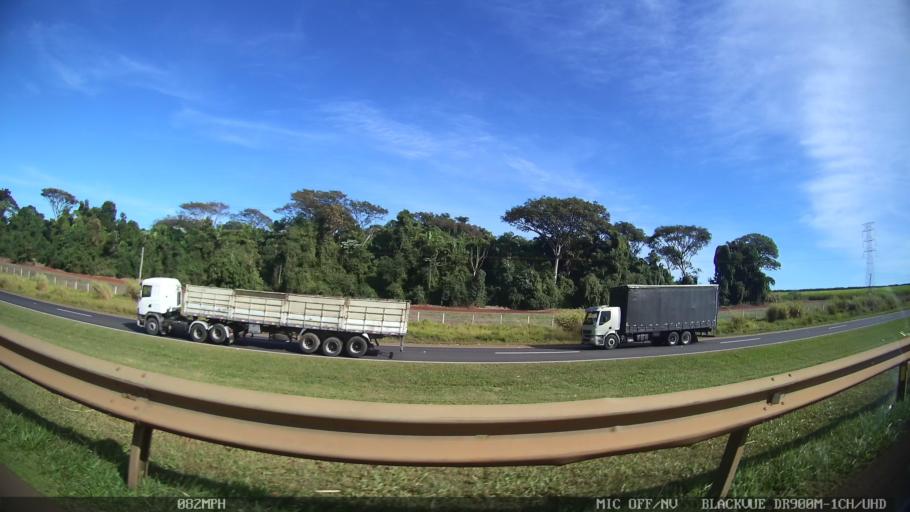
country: BR
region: Sao Paulo
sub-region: Araras
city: Araras
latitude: -22.3034
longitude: -47.3918
